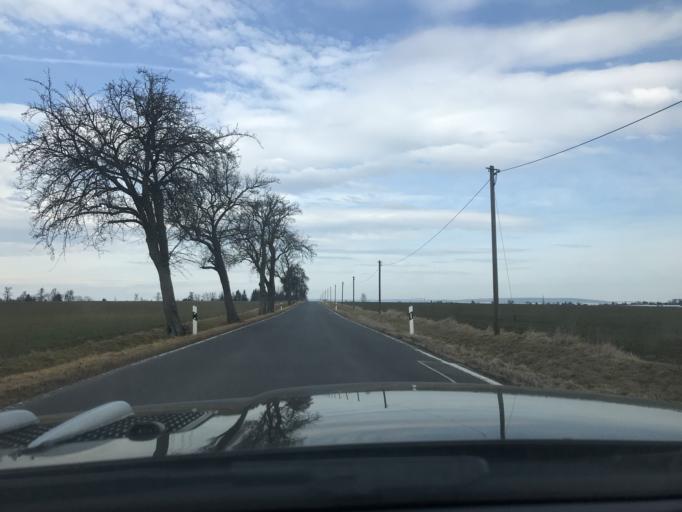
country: DE
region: Thuringia
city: Oberdorla
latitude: 51.1919
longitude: 10.4271
